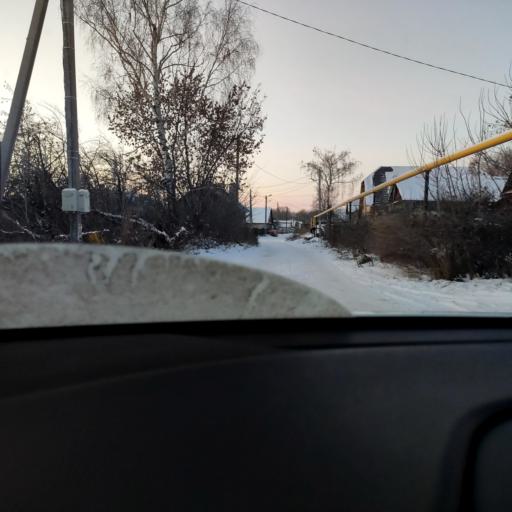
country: RU
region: Tatarstan
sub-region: Gorod Kazan'
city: Kazan
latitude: 55.7385
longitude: 49.0929
